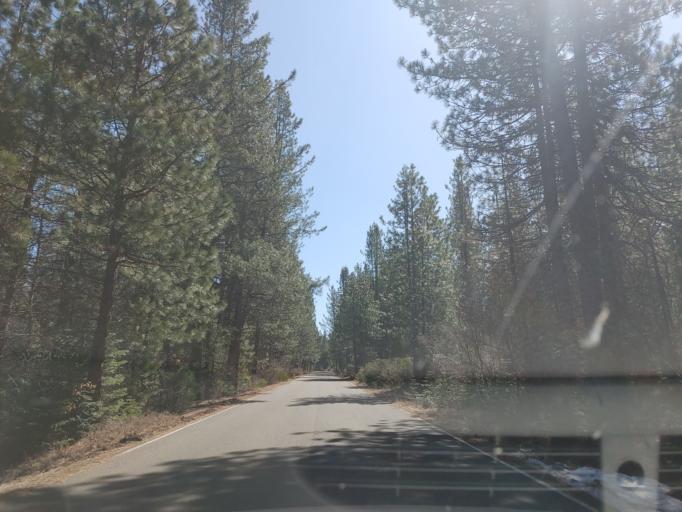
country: US
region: California
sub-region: Siskiyou County
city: McCloud
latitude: 41.2462
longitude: -122.0183
